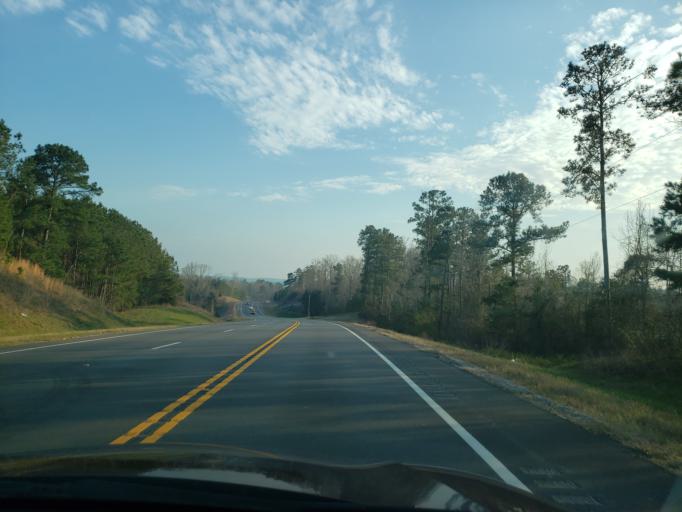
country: US
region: Alabama
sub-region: Hale County
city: Moundville
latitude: 32.8657
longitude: -87.6132
